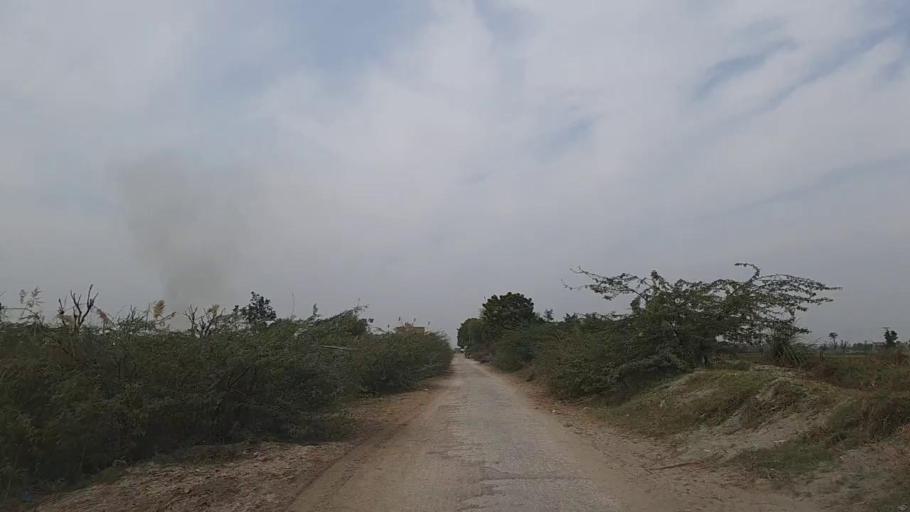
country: PK
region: Sindh
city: Daur
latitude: 26.4468
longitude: 68.4523
